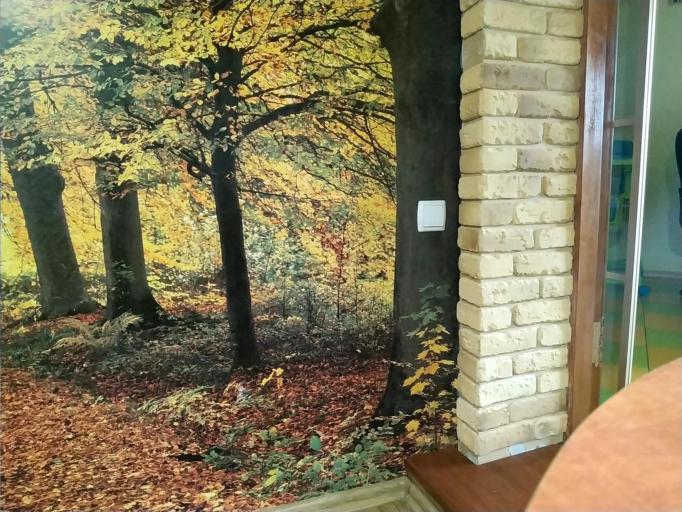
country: RU
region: Smolensk
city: Dorogobuzh
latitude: 54.9653
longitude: 33.2795
